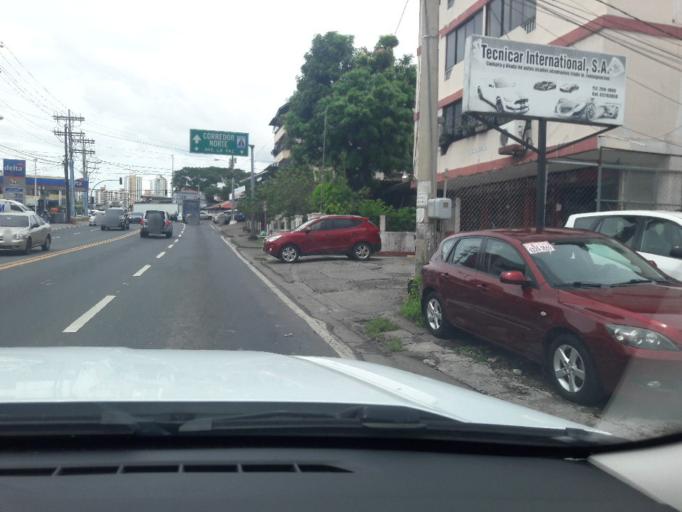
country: PA
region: Panama
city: Panama
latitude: 9.0149
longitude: -79.5221
